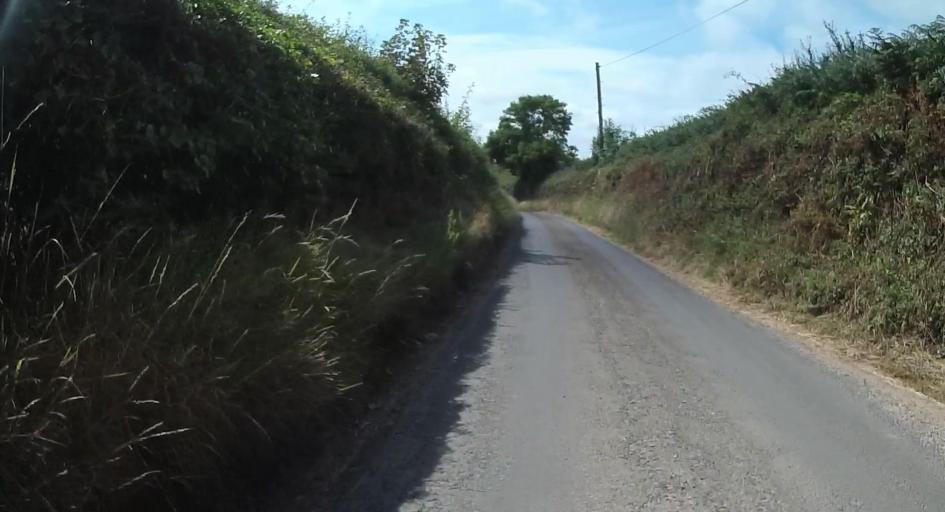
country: GB
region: England
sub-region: Dorset
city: Swanage
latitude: 50.6266
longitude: -1.9972
